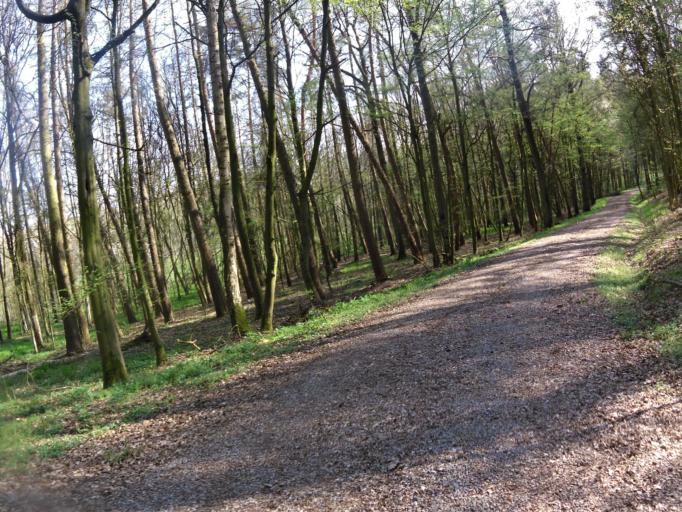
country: DE
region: Bavaria
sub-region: Regierungsbezirk Unterfranken
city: Rottendorf
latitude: 49.8206
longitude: 10.0649
